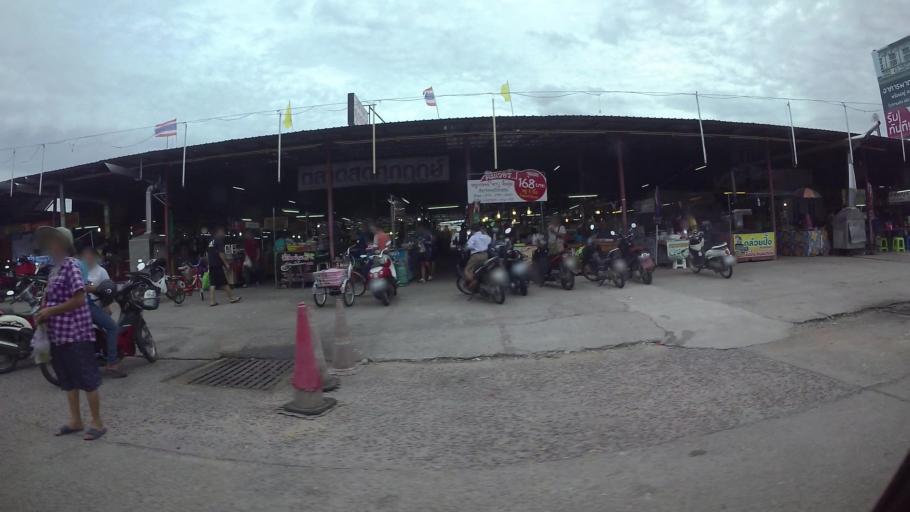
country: TH
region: Chon Buri
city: Si Racha
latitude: 13.1476
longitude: 100.9501
